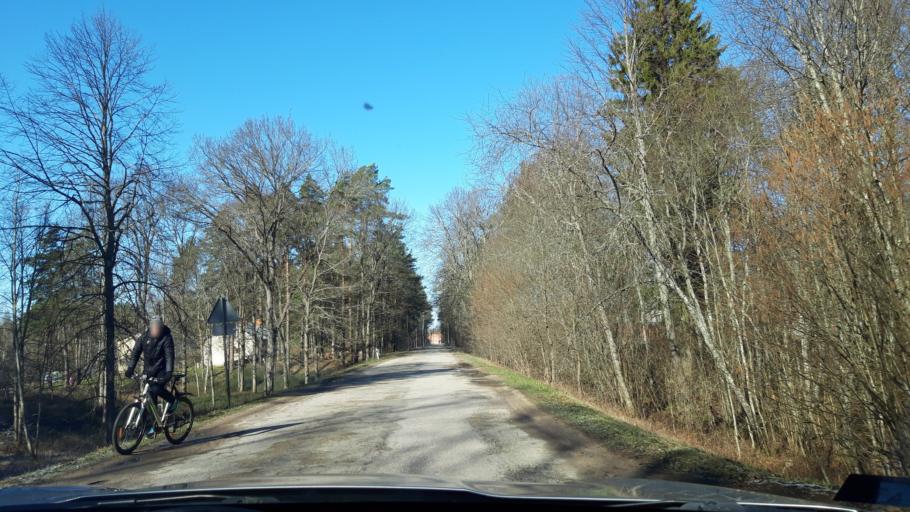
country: LV
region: Strenci
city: Strenci
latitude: 57.6201
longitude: 25.7012
